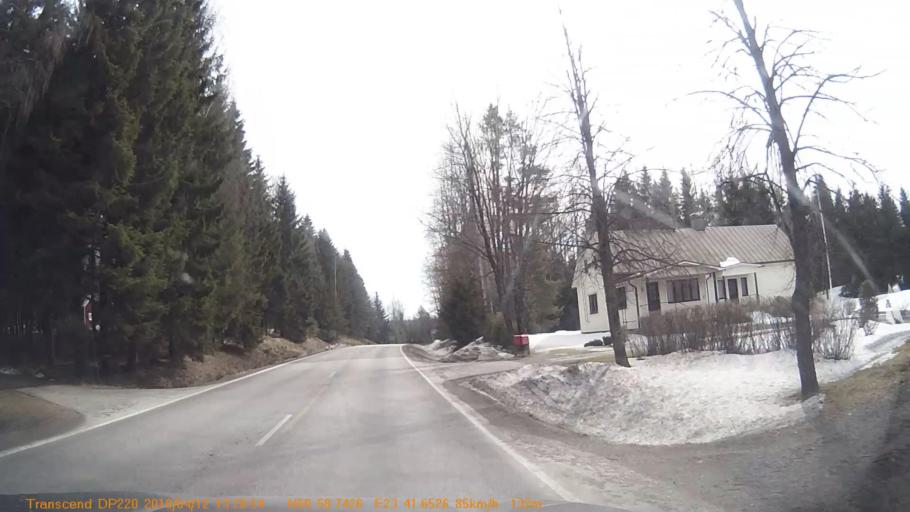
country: FI
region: Pirkanmaa
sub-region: Etelae-Pirkanmaa
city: Kylmaekoski
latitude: 60.9789
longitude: 23.6943
